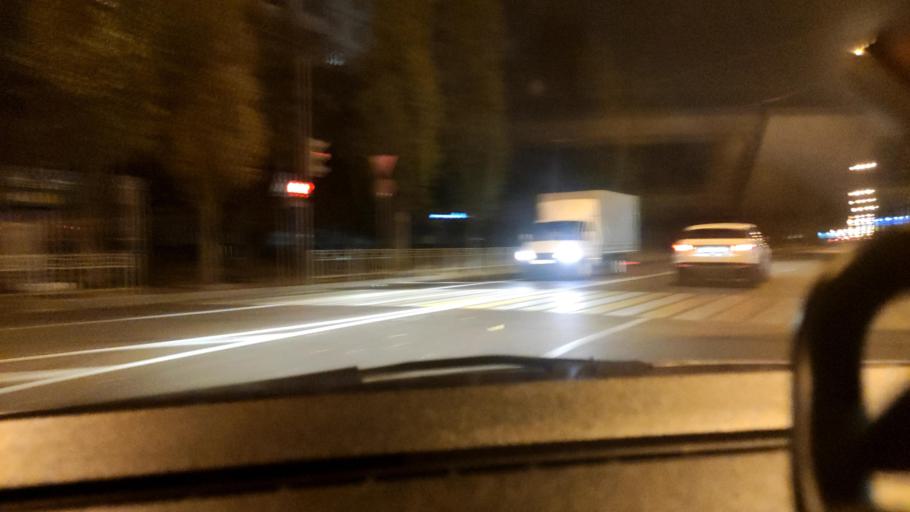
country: RU
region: Voronezj
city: Podgornoye
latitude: 51.7123
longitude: 39.1734
